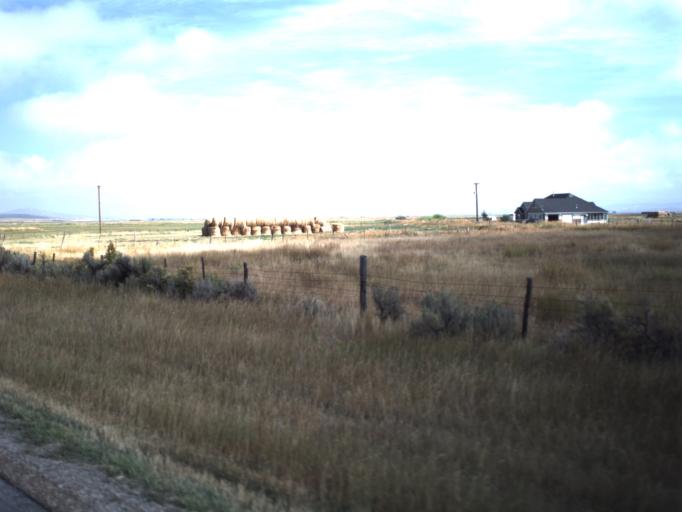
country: US
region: Utah
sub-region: Rich County
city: Randolph
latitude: 41.7134
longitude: -111.1594
